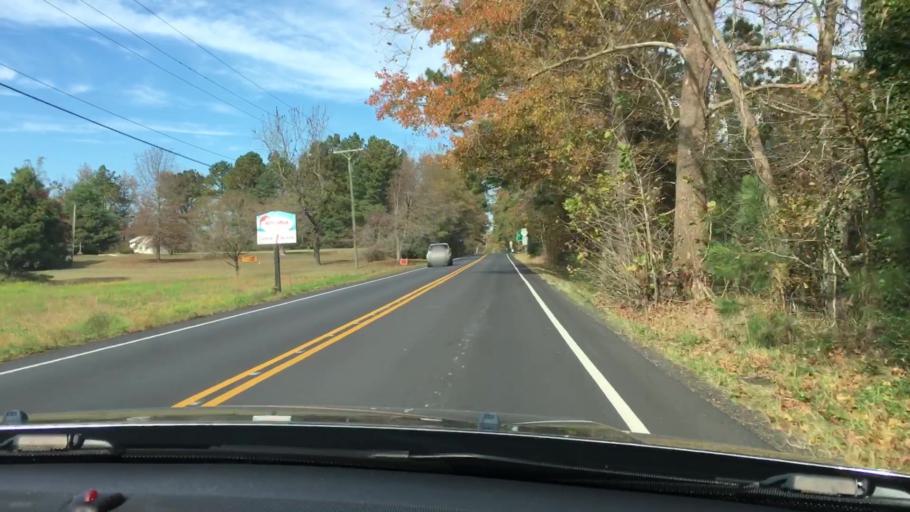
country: US
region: Virginia
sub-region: King William County
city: West Point
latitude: 37.4579
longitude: -76.8413
